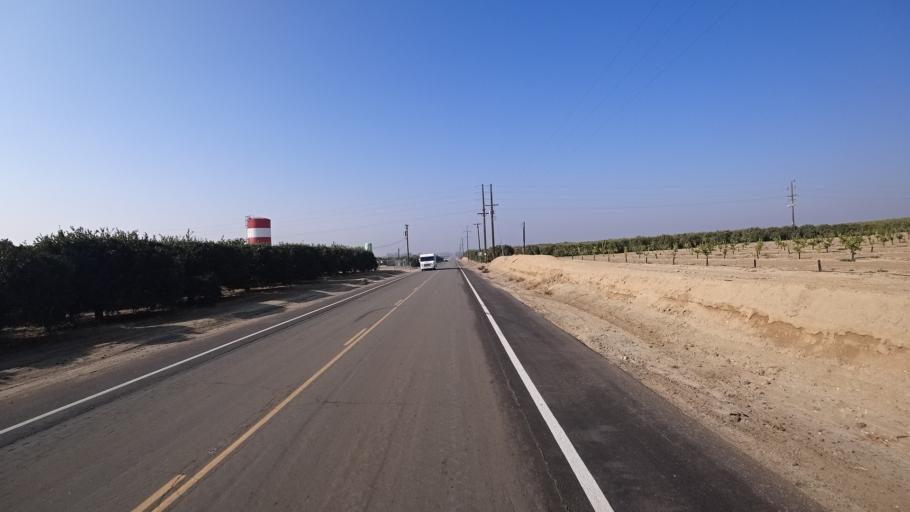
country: US
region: California
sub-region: Kern County
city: Lamont
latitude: 35.3618
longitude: -118.8779
